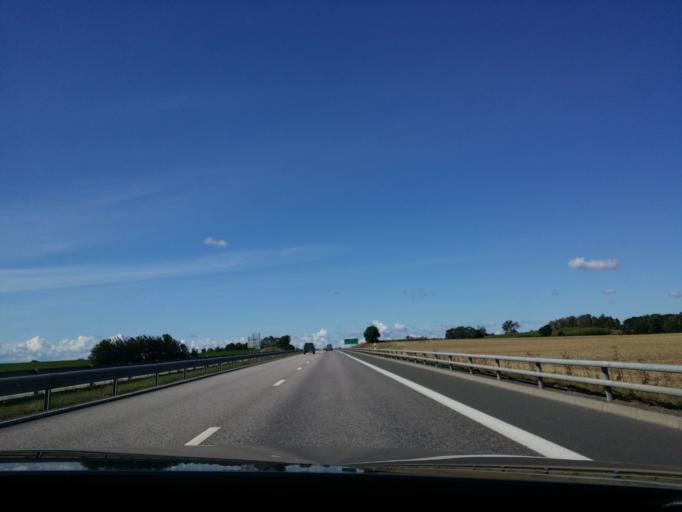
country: SE
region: Skane
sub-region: Kristianstads Kommun
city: Fjalkinge
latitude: 56.0328
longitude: 14.2525
